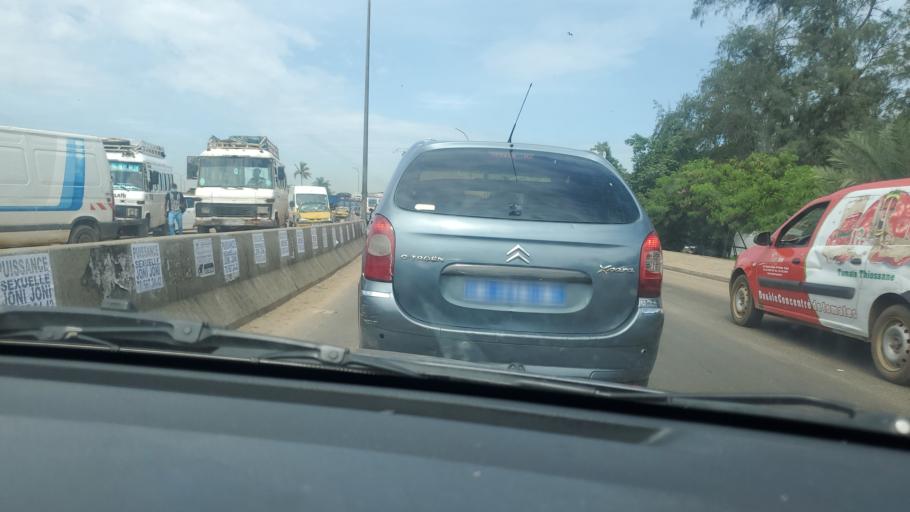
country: SN
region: Dakar
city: Pikine
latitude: 14.7458
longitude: -17.4236
